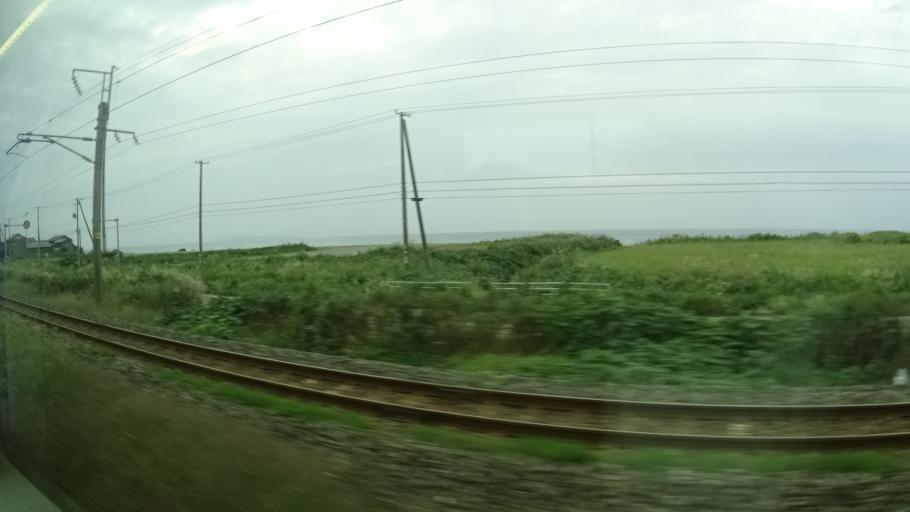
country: JP
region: Niigata
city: Murakami
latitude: 38.5338
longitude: 139.5457
